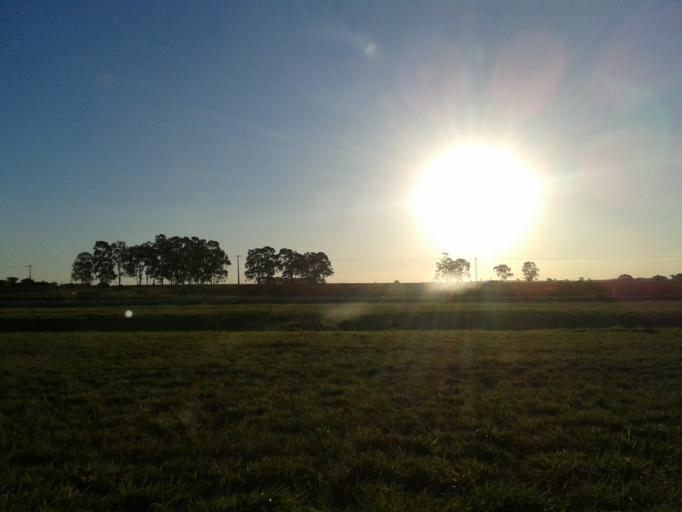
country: BR
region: Minas Gerais
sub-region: Centralina
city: Centralina
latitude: -18.7475
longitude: -49.2085
